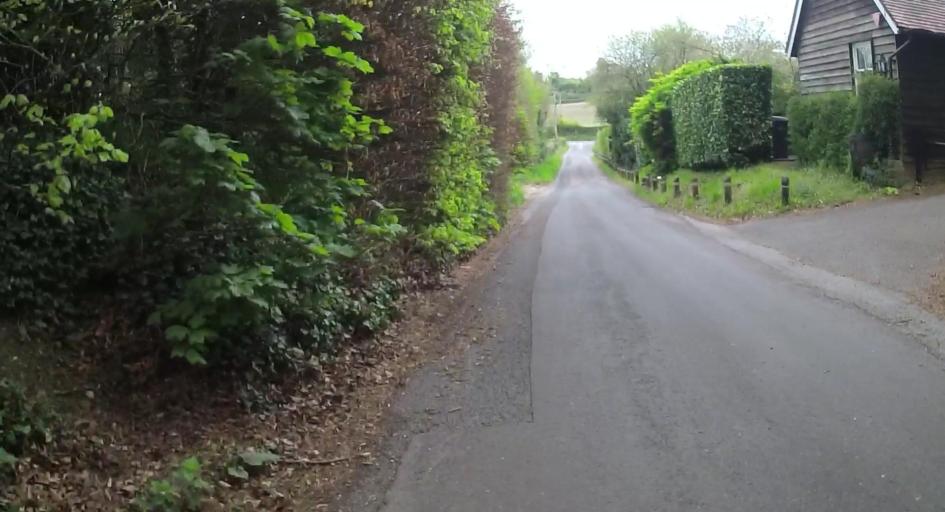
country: GB
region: England
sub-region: Hampshire
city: Colden Common
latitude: 51.0208
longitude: -1.3088
